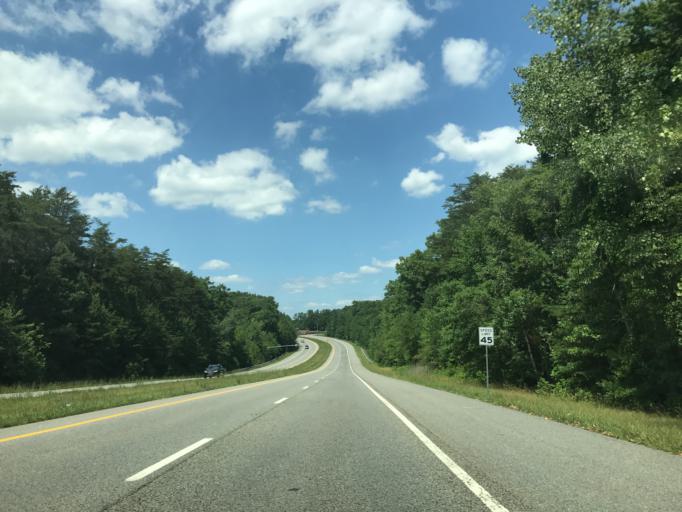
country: US
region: Maryland
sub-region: Prince George's County
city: Glenn Dale
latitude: 39.0107
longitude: -76.7629
